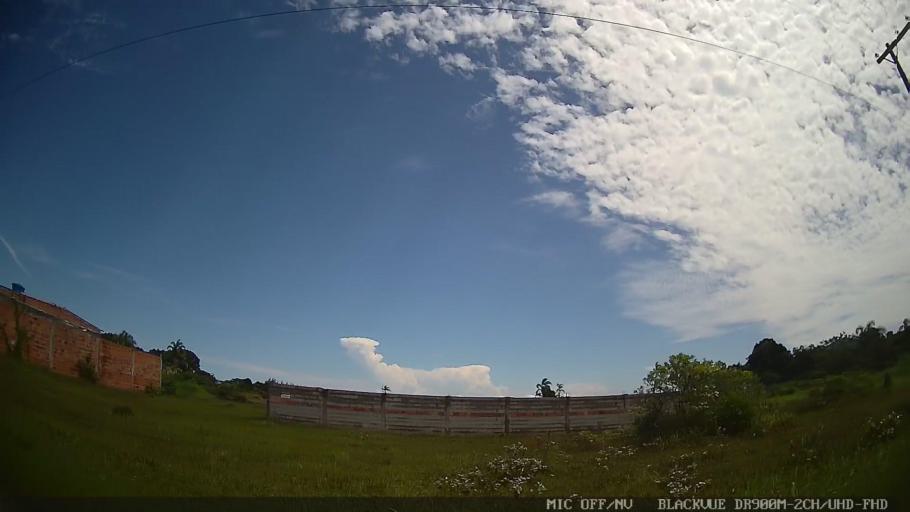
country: BR
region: Sao Paulo
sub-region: Iguape
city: Iguape
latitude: -24.7159
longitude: -47.5074
